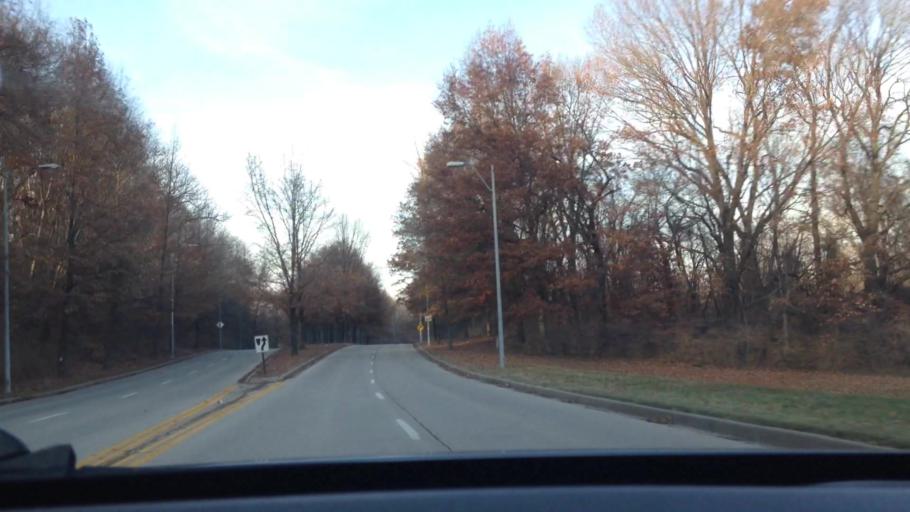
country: US
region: Missouri
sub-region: Clay County
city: Claycomo
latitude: 39.1569
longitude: -94.5169
